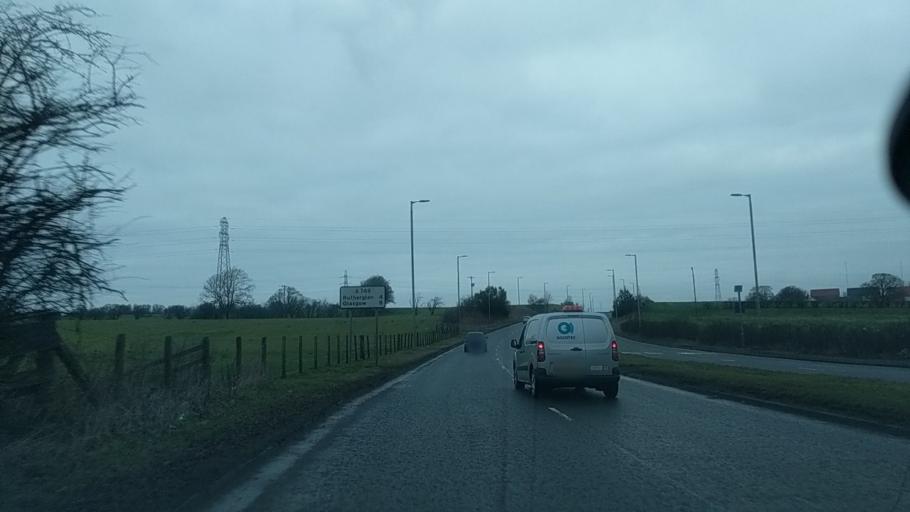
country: GB
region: Scotland
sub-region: South Lanarkshire
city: East Kilbride
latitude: 55.7858
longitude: -4.1667
